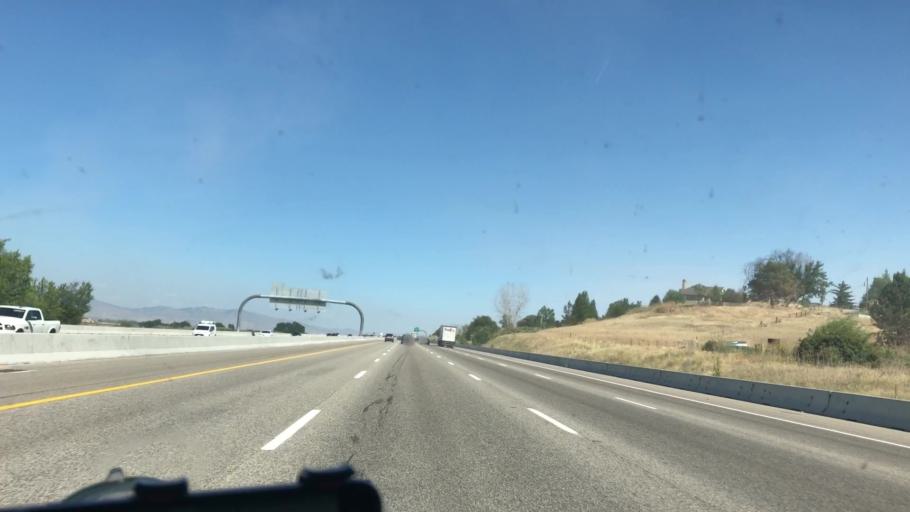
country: US
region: Idaho
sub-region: Ada County
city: Meridian
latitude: 43.5966
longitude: -116.4704
